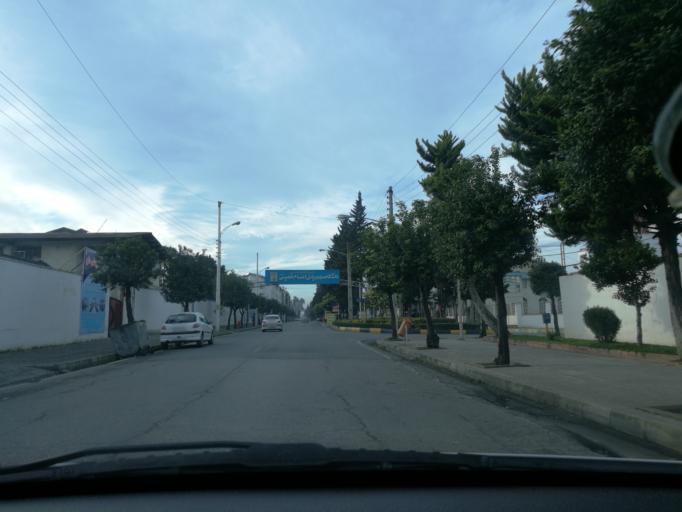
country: IR
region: Mazandaran
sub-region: Nowshahr
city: Nowshahr
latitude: 36.6527
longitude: 51.4998
